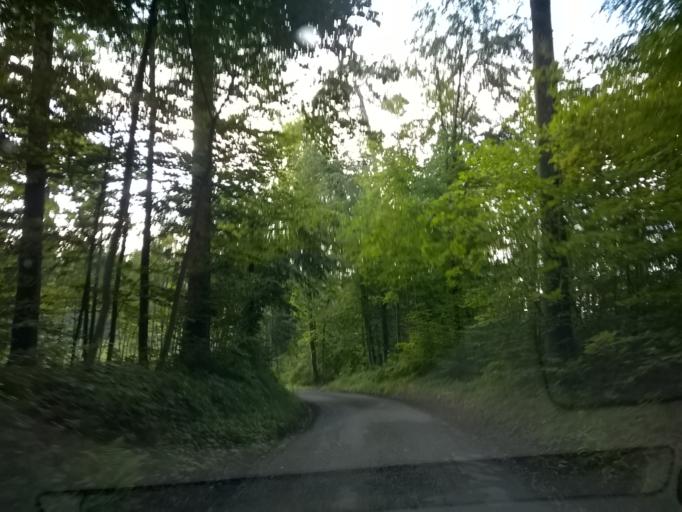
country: CH
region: Zurich
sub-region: Bezirk Buelach
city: Bachenbulach
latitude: 47.4995
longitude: 8.5655
